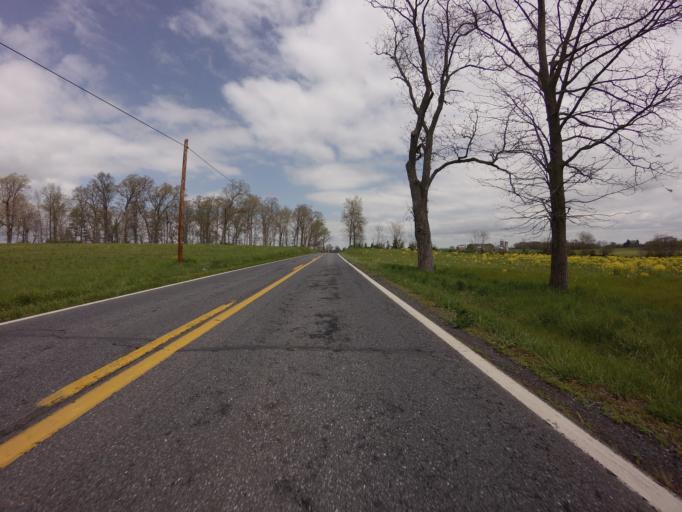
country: US
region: Maryland
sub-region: Frederick County
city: Thurmont
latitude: 39.5867
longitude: -77.3627
